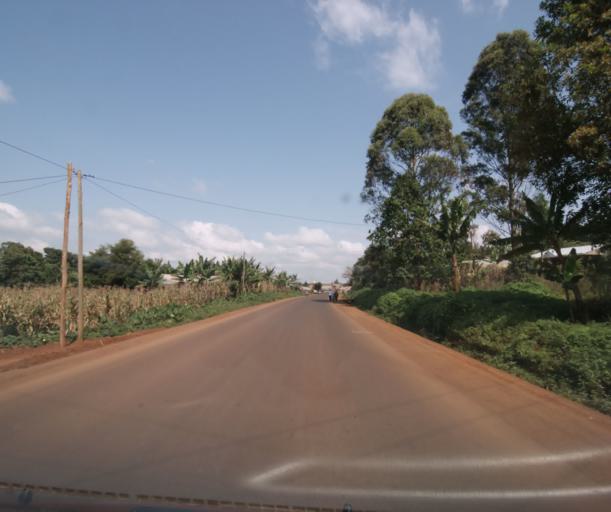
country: CM
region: West
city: Bansoa
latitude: 5.5000
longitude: 10.2458
